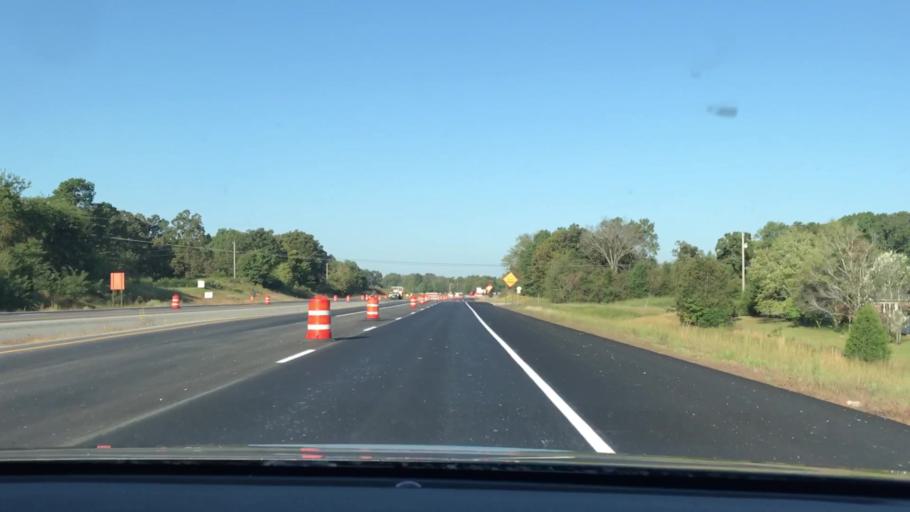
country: US
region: Kentucky
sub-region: Trigg County
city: Cadiz
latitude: 36.8385
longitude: -87.8497
